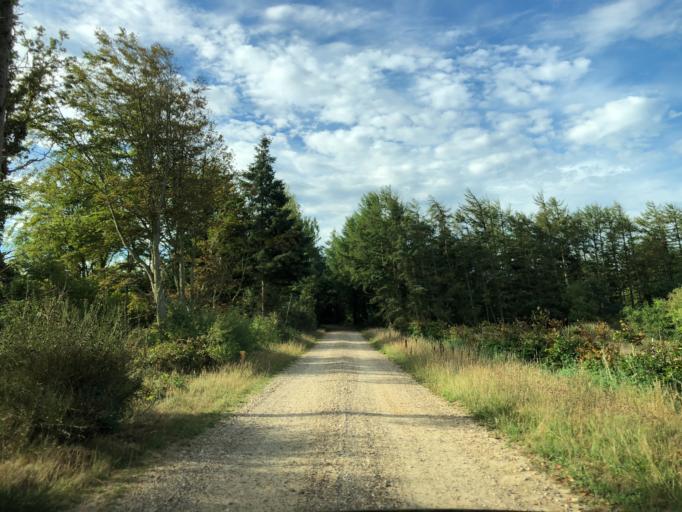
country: DK
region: Central Jutland
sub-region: Holstebro Kommune
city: Ulfborg
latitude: 56.1911
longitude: 8.3345
